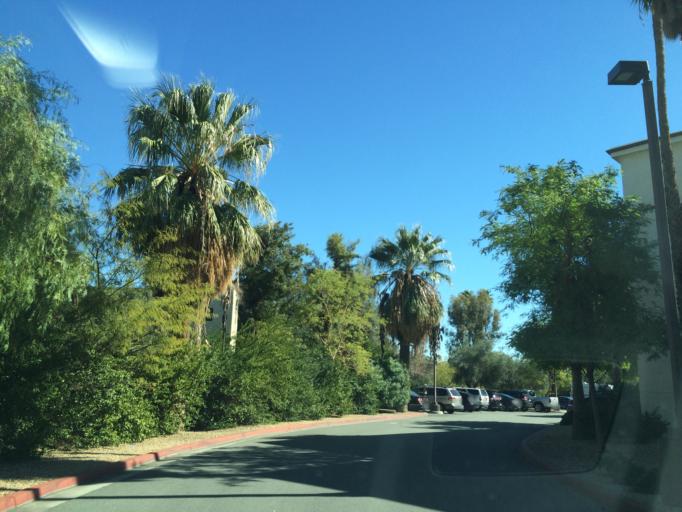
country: US
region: California
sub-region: Riverside County
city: Palm Springs
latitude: 33.8473
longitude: -116.5436
